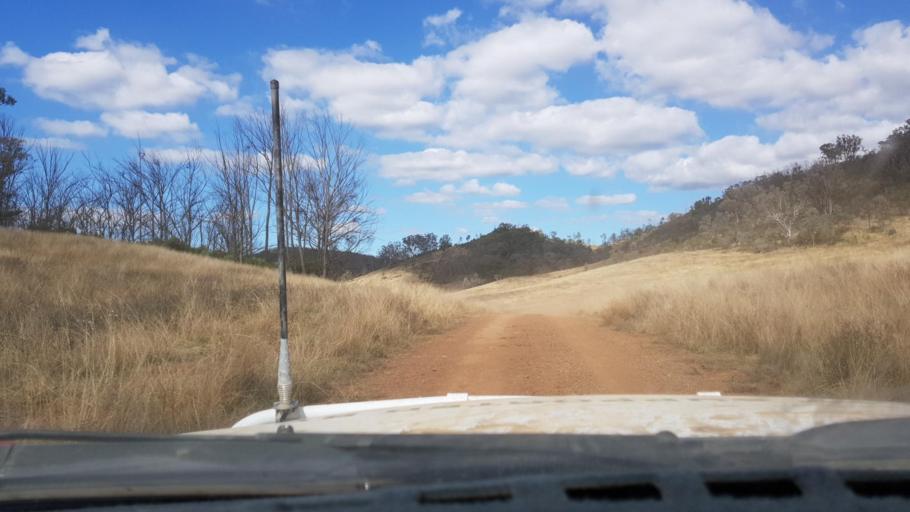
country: AU
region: New South Wales
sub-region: Tamworth Municipality
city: Manilla
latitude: -30.4368
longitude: 150.8275
